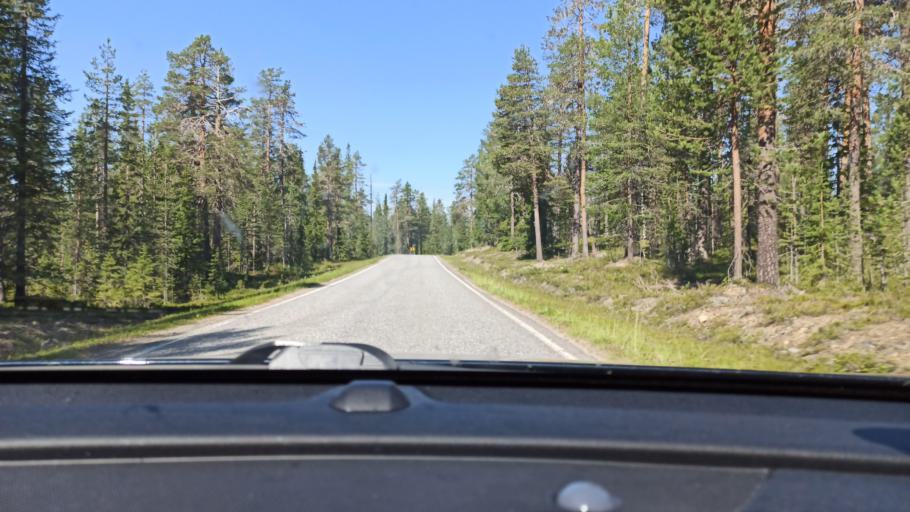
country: FI
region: Lapland
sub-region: Tunturi-Lappi
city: Kolari
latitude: 67.6701
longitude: 24.1531
